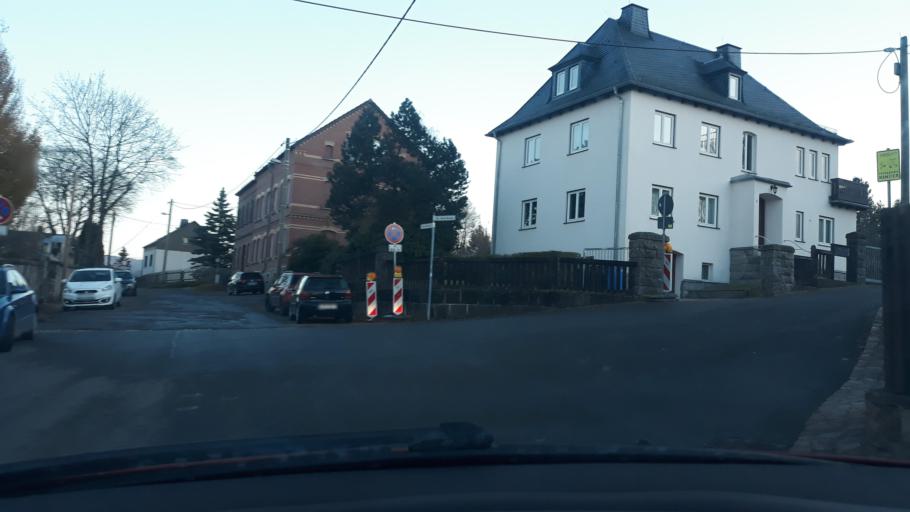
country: DE
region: Saxony
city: Kirchberg
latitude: 50.6190
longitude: 12.5296
